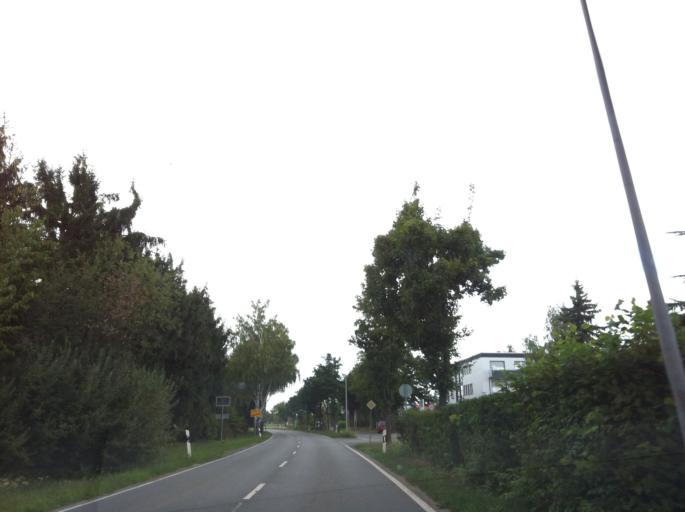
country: DE
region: Hesse
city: Pfungstadt
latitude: 49.8170
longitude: 8.5692
